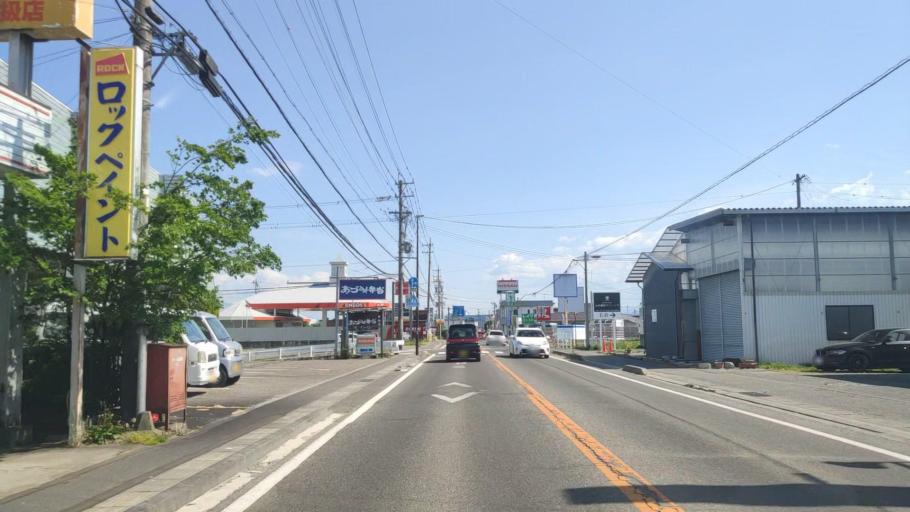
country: JP
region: Nagano
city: Hotaka
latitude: 36.3264
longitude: 137.8928
